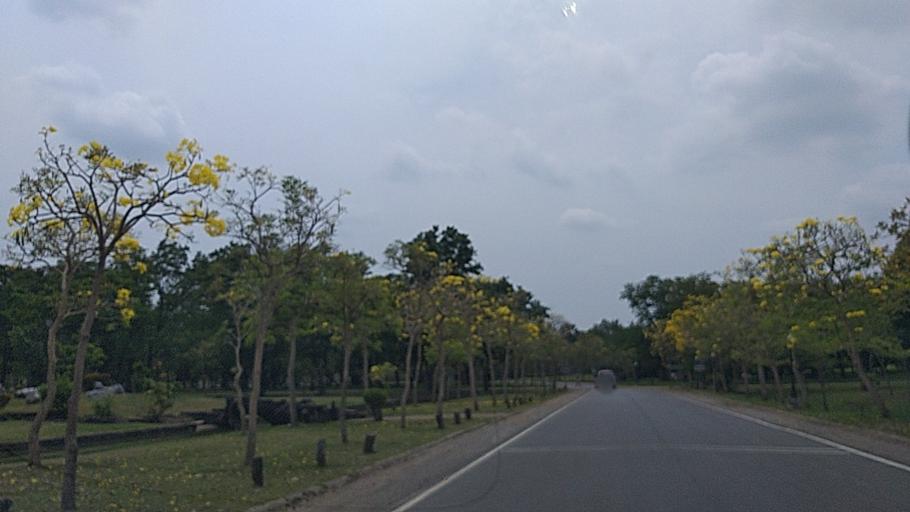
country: TH
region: Bangkok
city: Thawi Watthana
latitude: 13.7812
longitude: 100.3217
